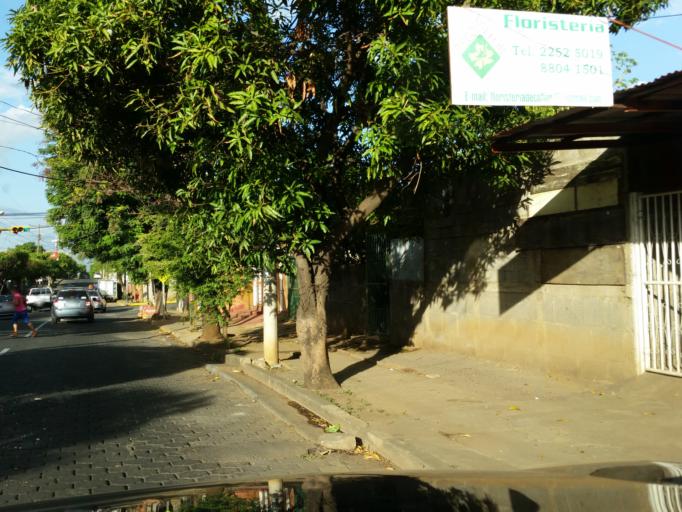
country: NI
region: Managua
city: Managua
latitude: 12.1266
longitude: -86.2516
